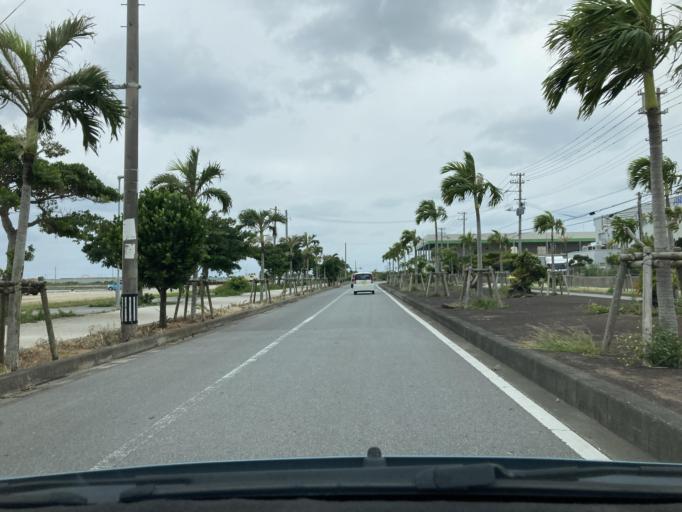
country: JP
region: Okinawa
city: Itoman
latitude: 26.1364
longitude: 127.6562
